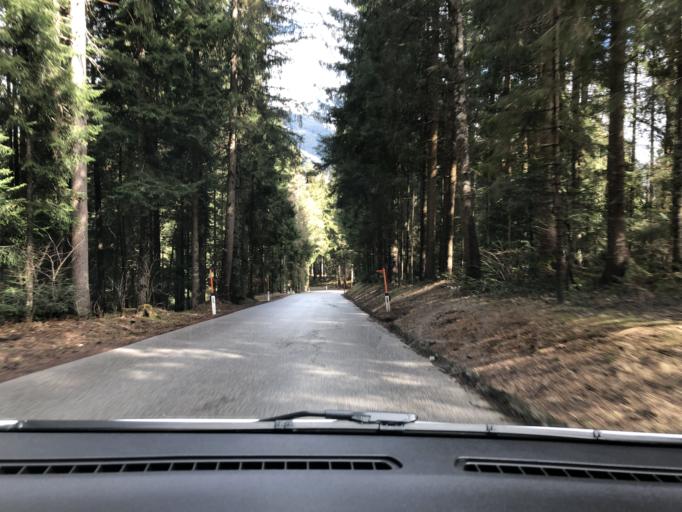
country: AT
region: Tyrol
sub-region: Politischer Bezirk Kitzbuhel
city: Hopfgarten im Brixental
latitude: 47.4471
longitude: 12.1476
